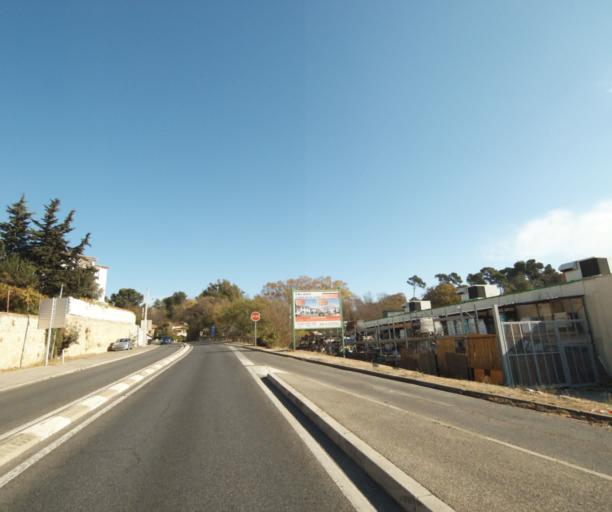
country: FR
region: Provence-Alpes-Cote d'Azur
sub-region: Departement des Bouches-du-Rhone
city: Plan-de-Cuques
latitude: 43.3353
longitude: 5.4542
